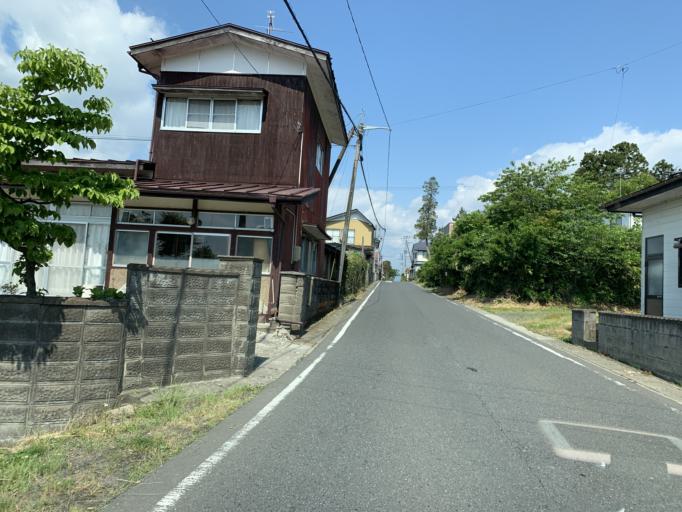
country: JP
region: Iwate
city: Ichinoseki
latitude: 38.7958
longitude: 141.0243
